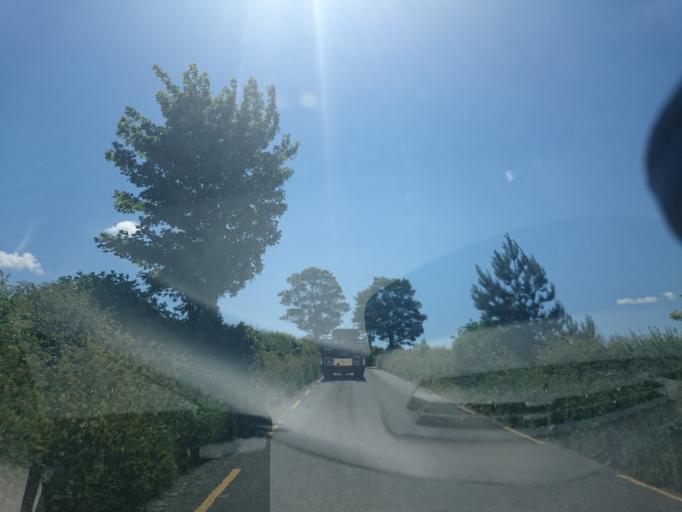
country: IE
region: Leinster
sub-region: Kilkenny
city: Graiguenamanagh
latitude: 52.6080
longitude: -6.9926
